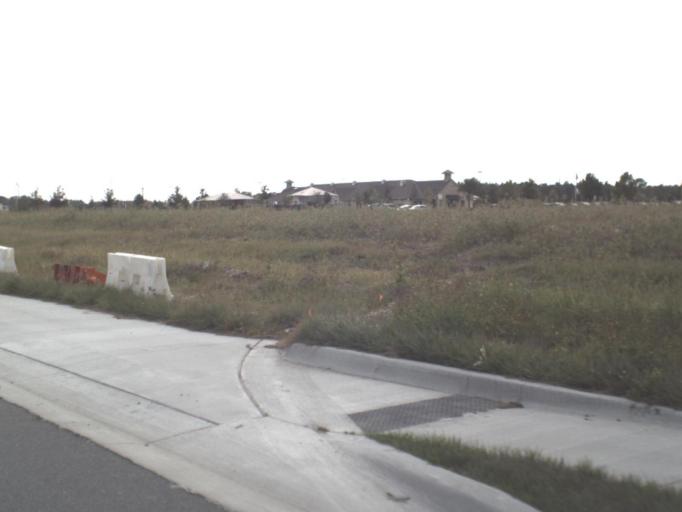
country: US
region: Florida
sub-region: Osceola County
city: Buenaventura Lakes
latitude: 28.3881
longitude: -81.2445
